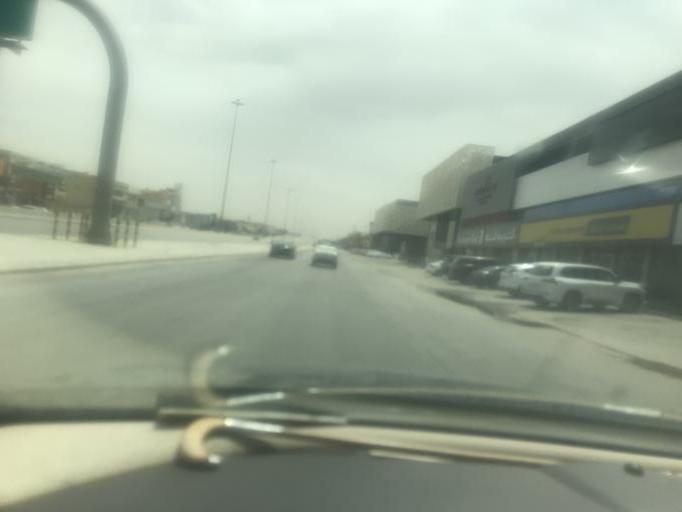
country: SA
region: Ar Riyad
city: Riyadh
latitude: 24.7968
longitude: 46.6981
